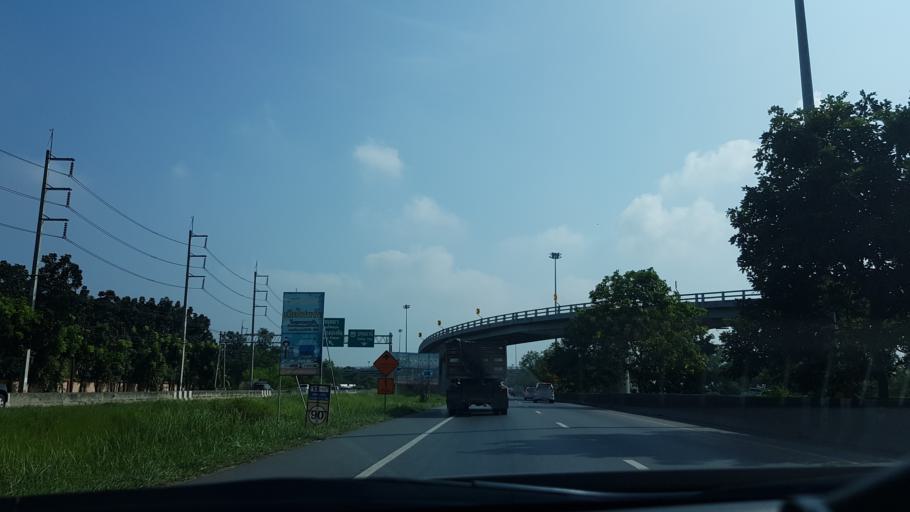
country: TH
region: Phra Nakhon Si Ayutthaya
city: Bang Pa-in
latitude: 14.1554
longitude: 100.5653
